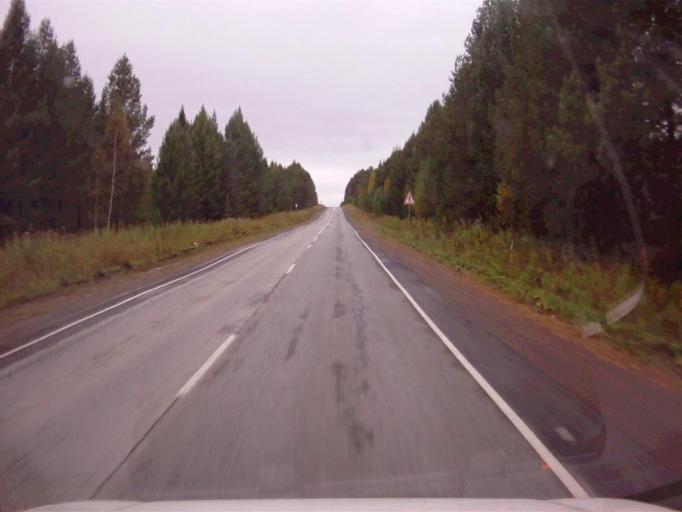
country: RU
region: Chelyabinsk
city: Nyazepetrovsk
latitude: 56.0666
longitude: 59.6787
